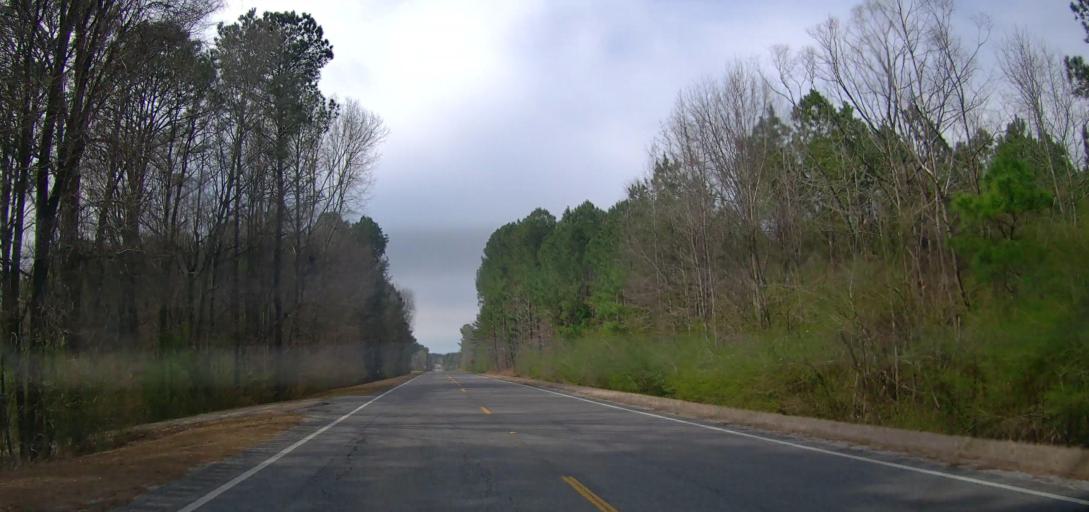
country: US
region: Alabama
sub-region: Walker County
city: Carbon Hill
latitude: 33.9033
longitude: -87.5490
